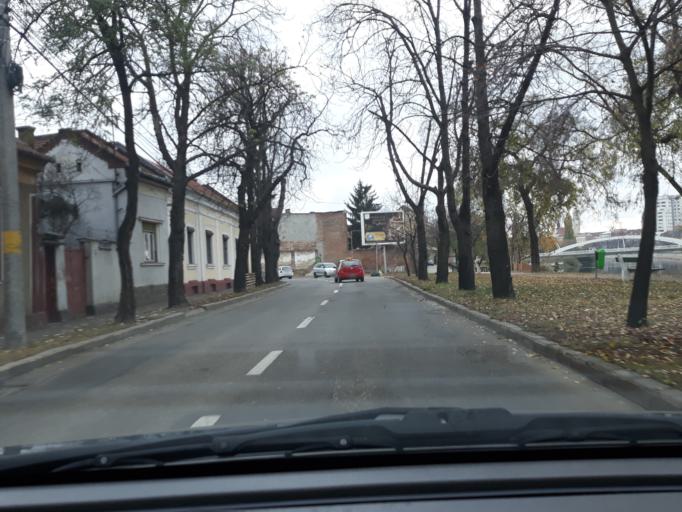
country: RO
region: Bihor
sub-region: Comuna Biharea
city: Oradea
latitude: 47.0637
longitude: 21.9252
